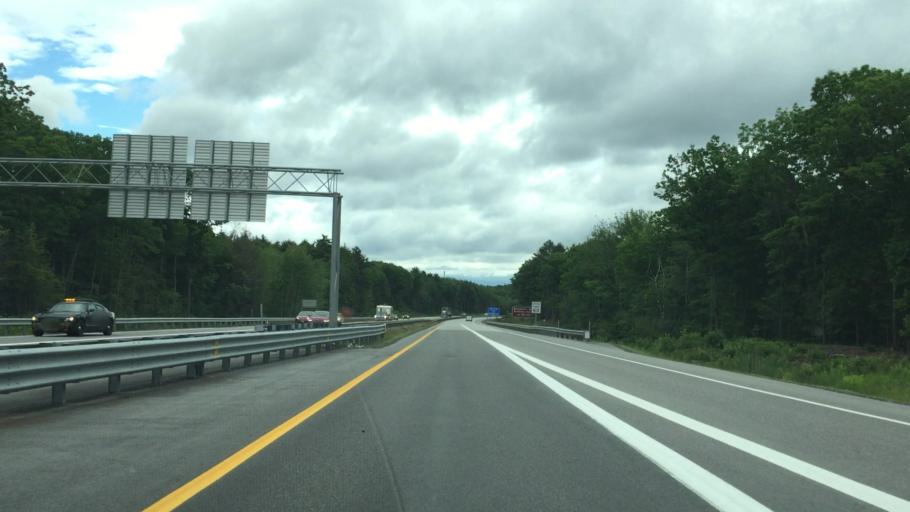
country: US
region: Maine
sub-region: Cumberland County
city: Falmouth
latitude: 43.7337
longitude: -70.2515
